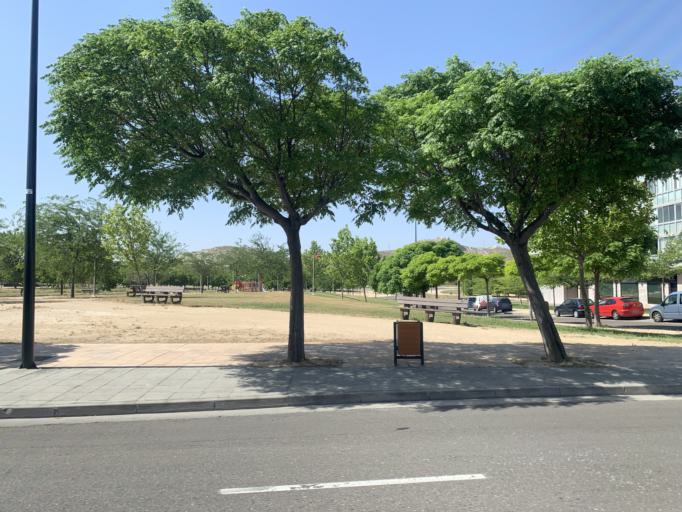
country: ES
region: Aragon
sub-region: Provincia de Zaragoza
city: Montecanal
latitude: 41.6239
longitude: -0.9350
